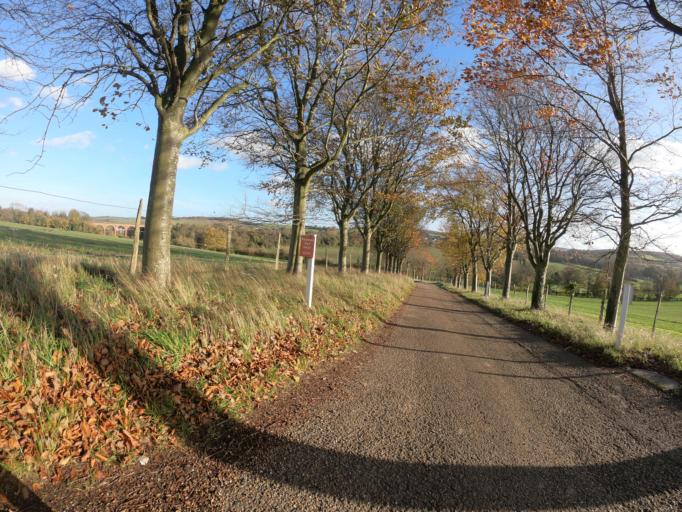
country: GB
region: England
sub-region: Kent
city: Eynsford
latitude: 51.3680
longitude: 0.1977
